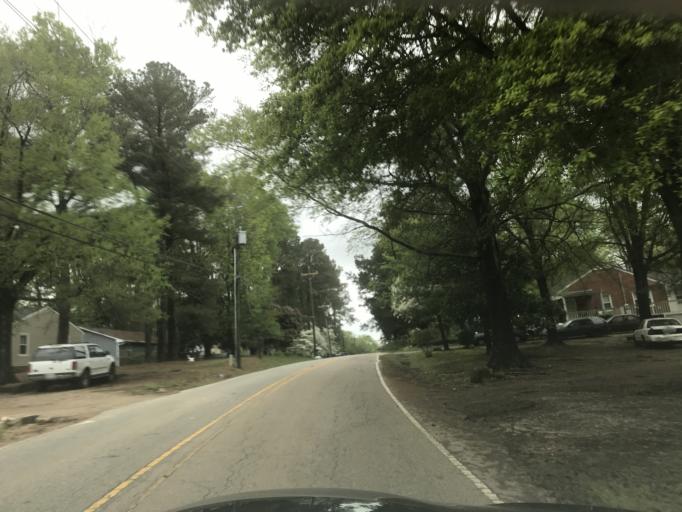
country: US
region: North Carolina
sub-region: Wake County
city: Raleigh
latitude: 35.7470
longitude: -78.6575
